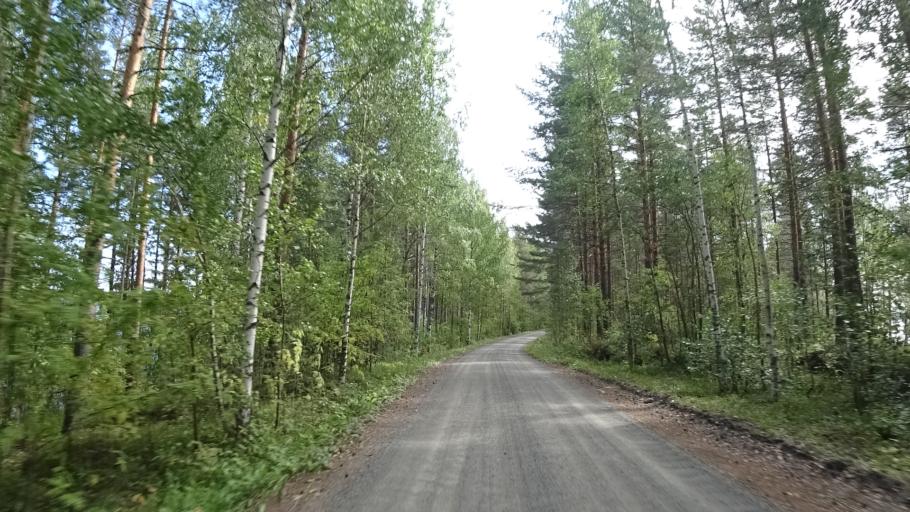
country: FI
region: North Karelia
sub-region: Keski-Karjala
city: Raeaekkylae
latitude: 62.3926
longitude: 29.7727
